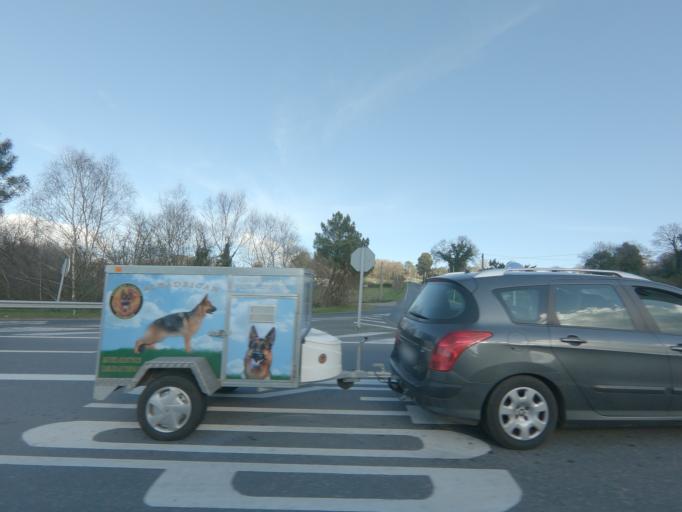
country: ES
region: Galicia
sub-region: Provincia de Pontevedra
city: Silleda
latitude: 42.7053
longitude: -8.2589
